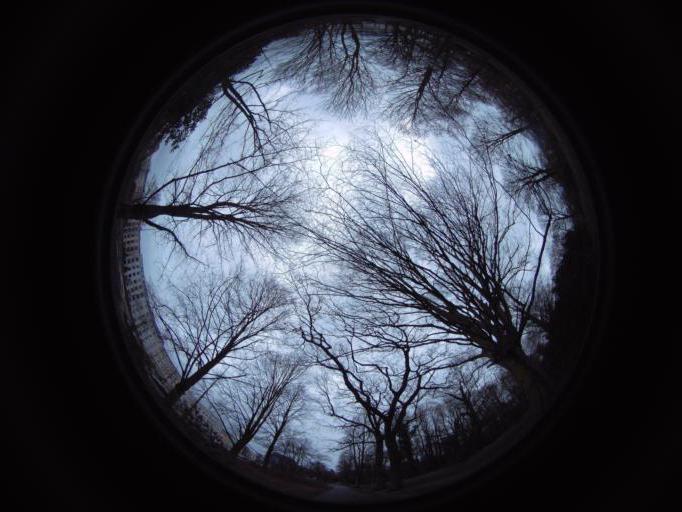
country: DE
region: Mecklenburg-Vorpommern
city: Rostock
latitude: 54.0847
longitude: 12.1167
